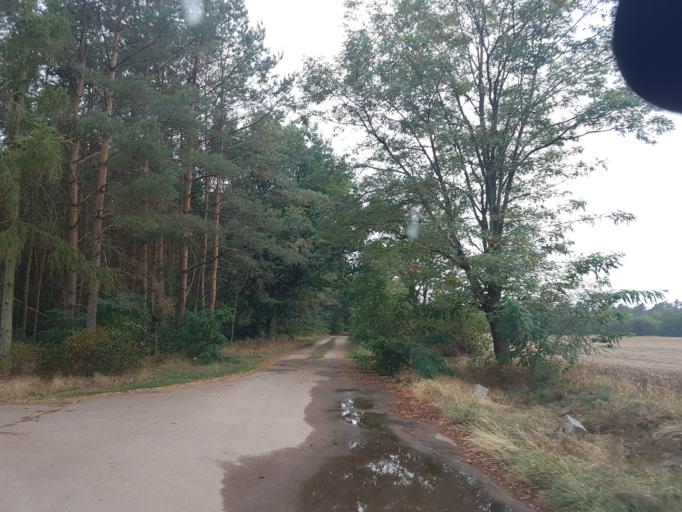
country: DE
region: Saxony-Anhalt
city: Klieken
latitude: 51.9665
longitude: 12.3354
